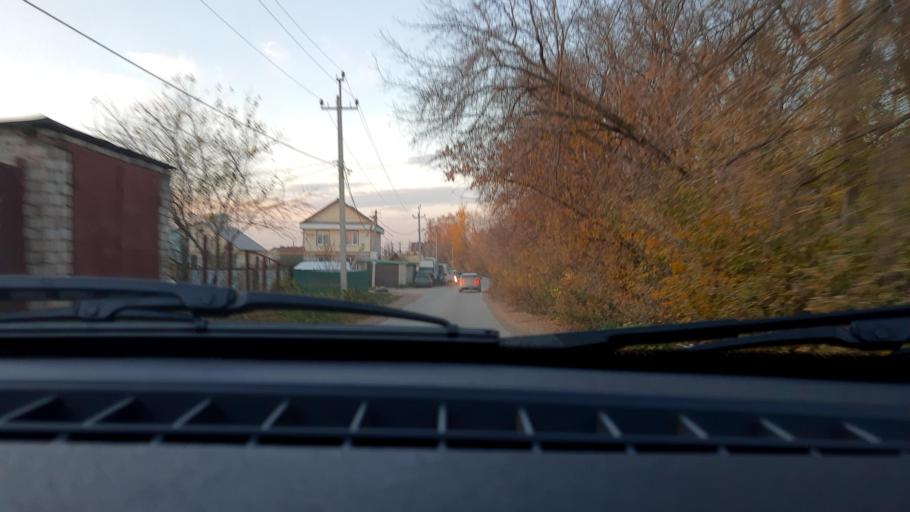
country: RU
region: Bashkortostan
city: Mikhaylovka
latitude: 54.7614
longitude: 55.9134
